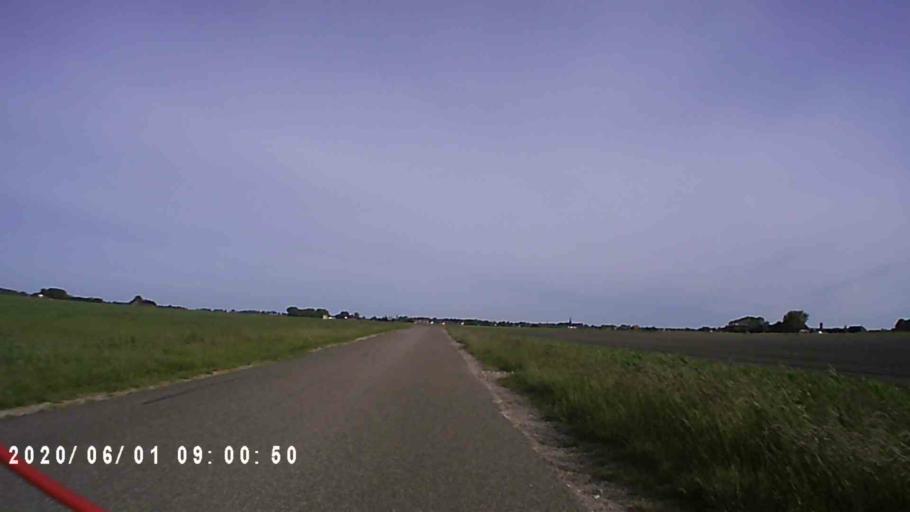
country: NL
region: Friesland
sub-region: Gemeente Ferwerderadiel
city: Hallum
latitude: 53.2883
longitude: 5.7950
